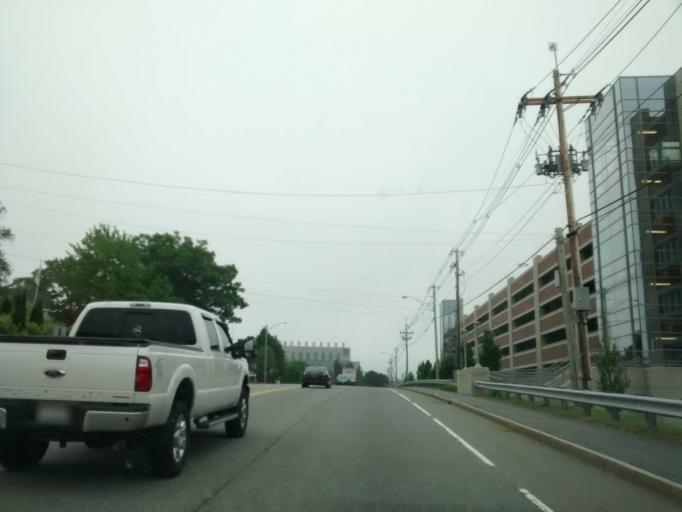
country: US
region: Massachusetts
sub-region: Worcester County
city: Hamilton
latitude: 42.2834
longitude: -71.7629
